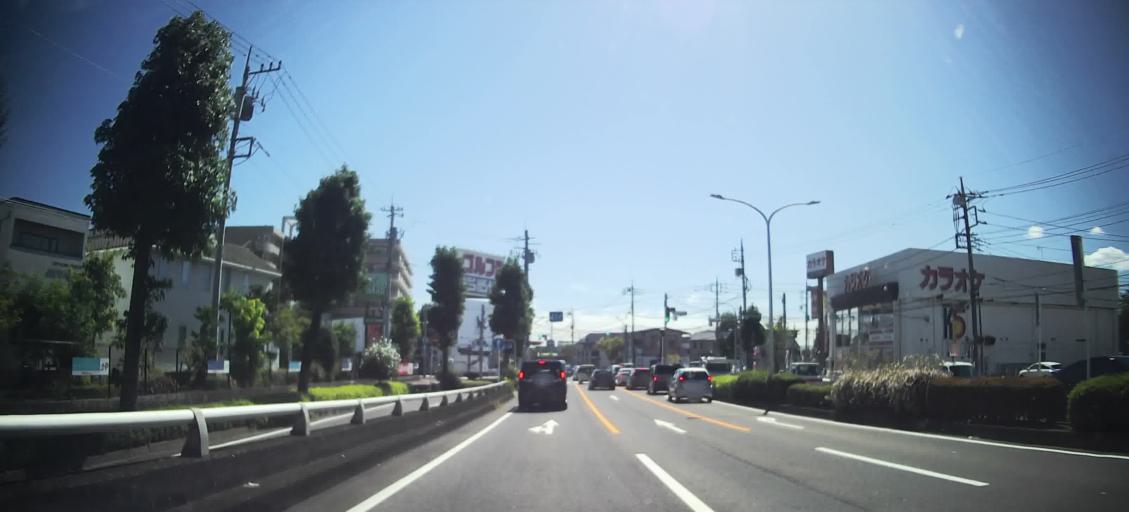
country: JP
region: Gunma
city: Maebashi-shi
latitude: 36.3750
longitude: 139.0435
